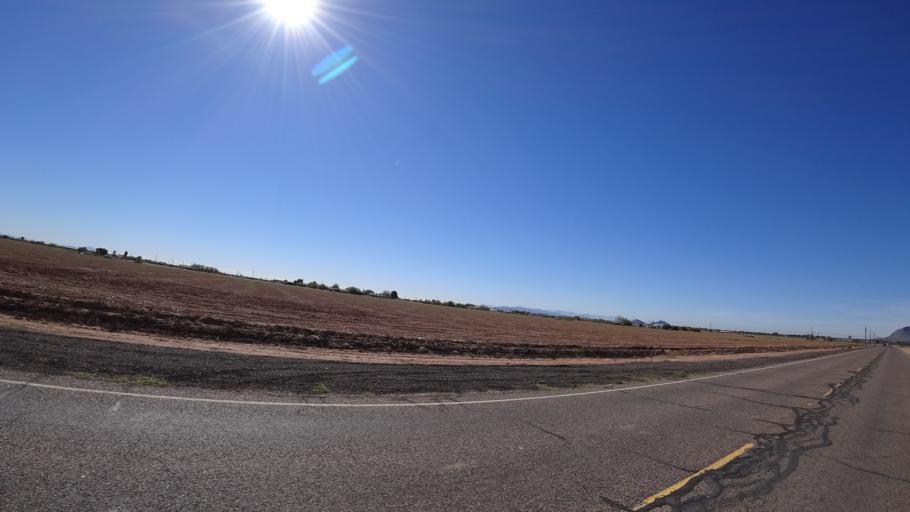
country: US
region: Arizona
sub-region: Maricopa County
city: Scottsdale
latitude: 33.5096
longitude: -111.8618
